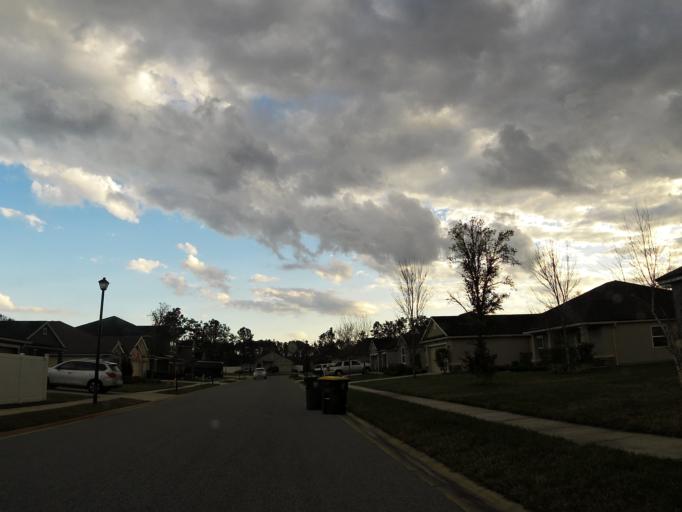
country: US
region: Florida
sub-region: Saint Johns County
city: Fruit Cove
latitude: 30.1718
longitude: -81.5672
